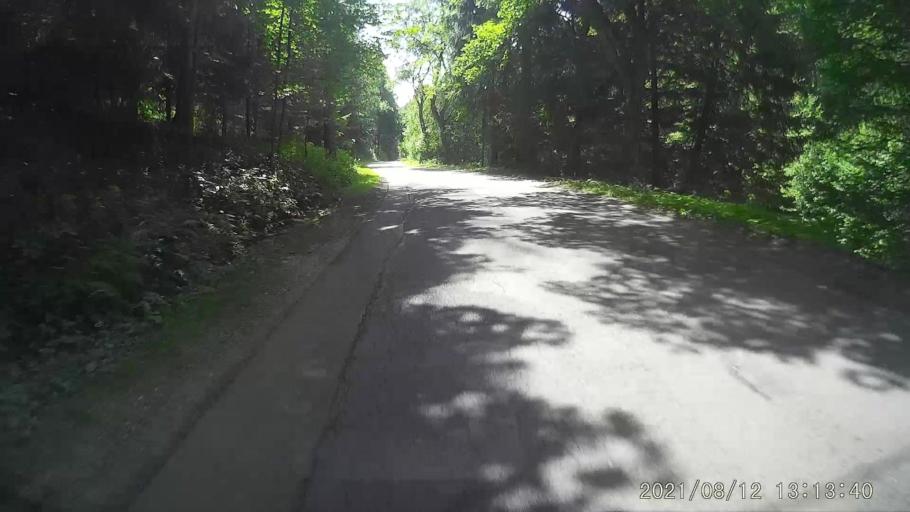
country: PL
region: Lower Silesian Voivodeship
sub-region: Powiat klodzki
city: Stronie Slaskie
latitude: 50.2550
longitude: 16.8546
